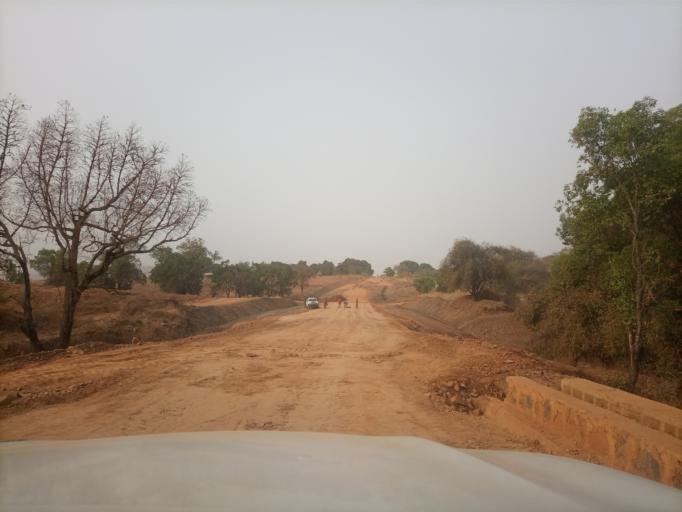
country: ET
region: Oromiya
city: Mendi
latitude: 10.2118
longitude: 35.0820
